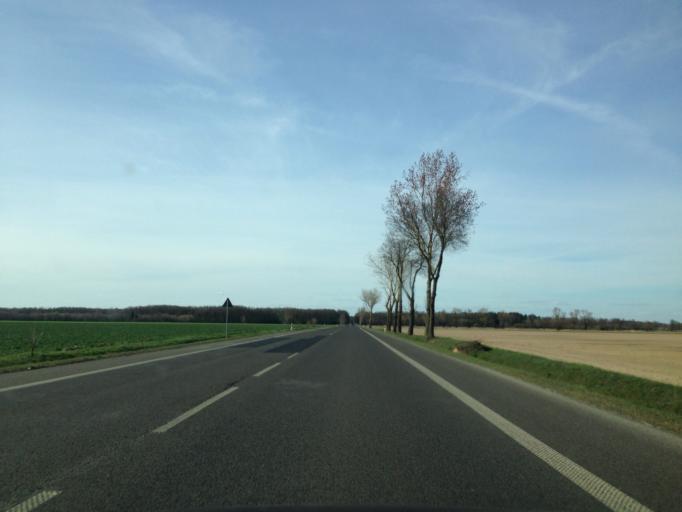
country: PL
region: Lodz Voivodeship
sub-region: Powiat kutnowski
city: Ostrowy
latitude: 52.3378
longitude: 19.1485
